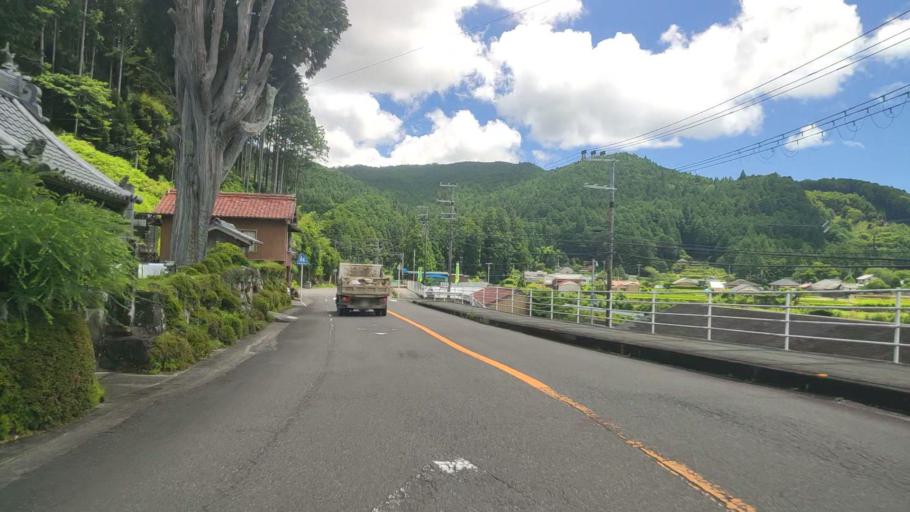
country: JP
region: Mie
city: Owase
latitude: 33.9493
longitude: 136.0723
